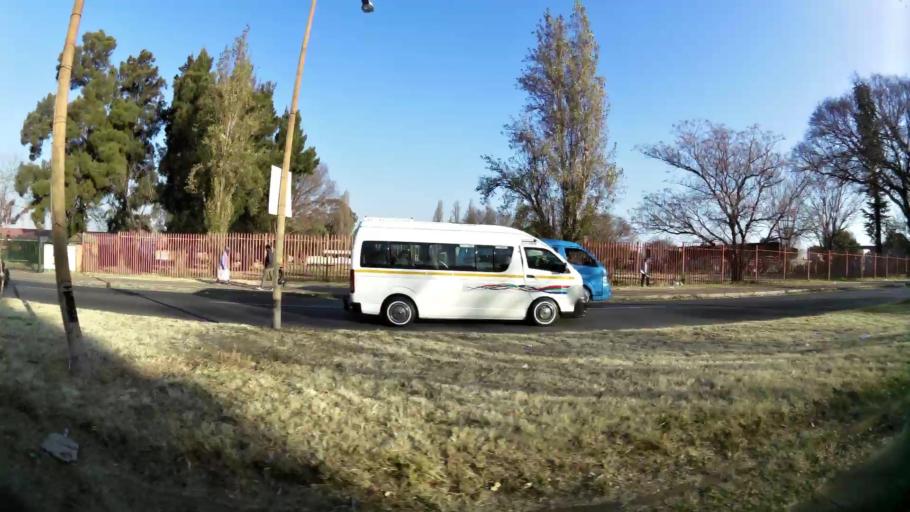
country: ZA
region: Gauteng
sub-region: City of Johannesburg Metropolitan Municipality
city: Soweto
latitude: -26.2521
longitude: 27.8793
